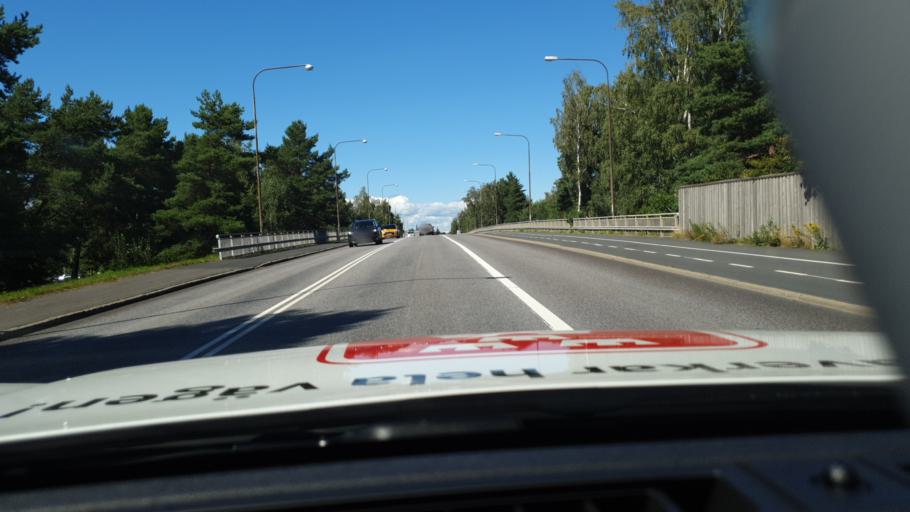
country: SE
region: Joenkoeping
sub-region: Jonkopings Kommun
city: Jonkoping
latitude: 57.7580
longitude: 14.1689
